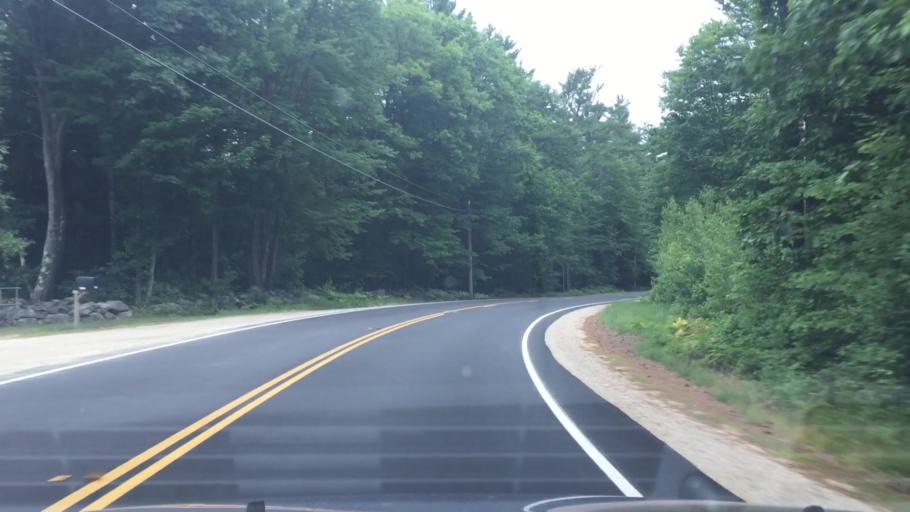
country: US
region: New Hampshire
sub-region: Carroll County
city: Freedom
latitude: 43.8191
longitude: -71.0669
